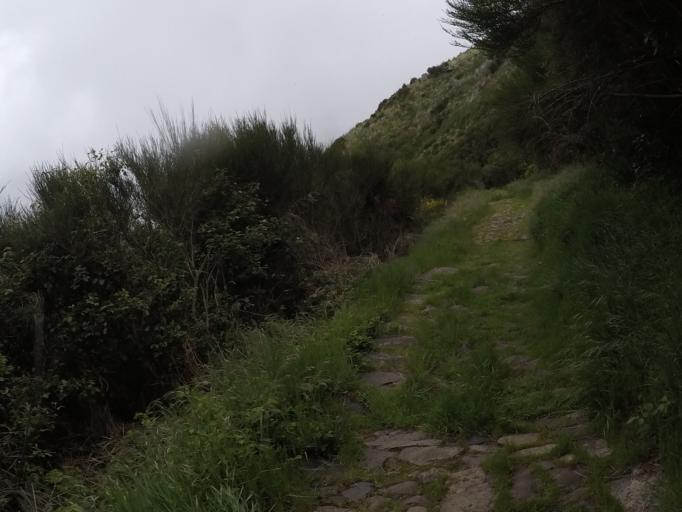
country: PT
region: Madeira
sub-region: Camara de Lobos
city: Curral das Freiras
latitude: 32.7125
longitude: -16.9884
